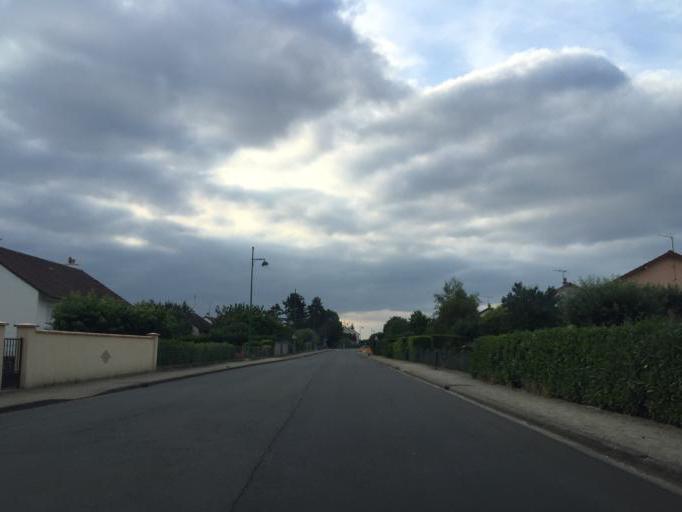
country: FR
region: Auvergne
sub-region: Departement de l'Allier
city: Yzeure
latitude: 46.5541
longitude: 3.3632
